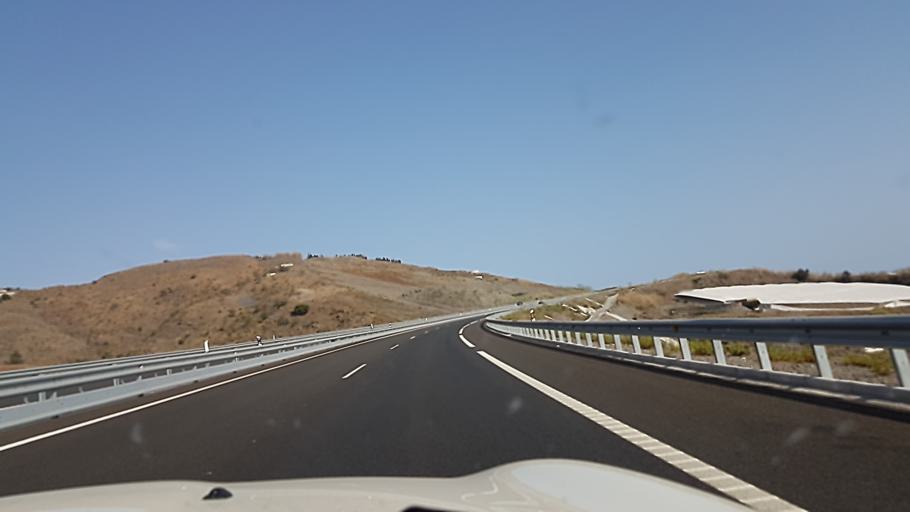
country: ES
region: Andalusia
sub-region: Provincia de Granada
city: Albunol
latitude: 36.7553
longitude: -3.2217
